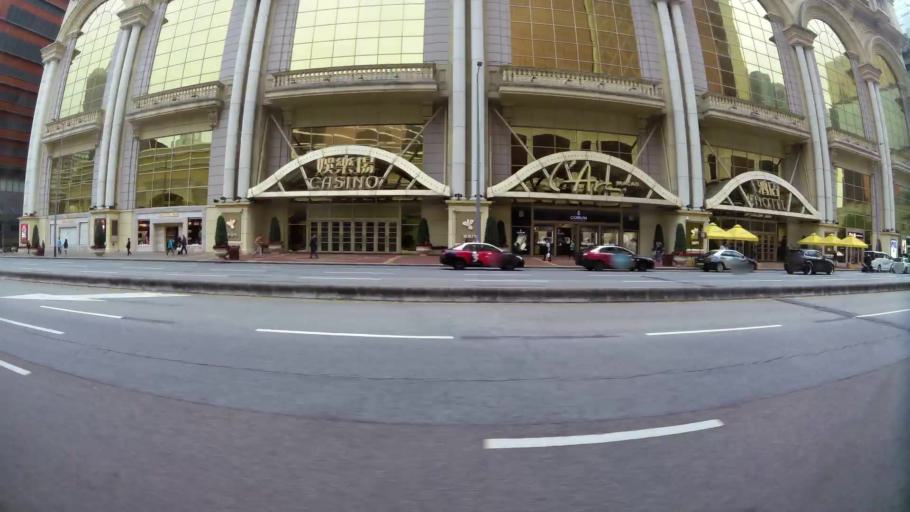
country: MO
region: Macau
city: Macau
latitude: 22.1884
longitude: 113.5477
